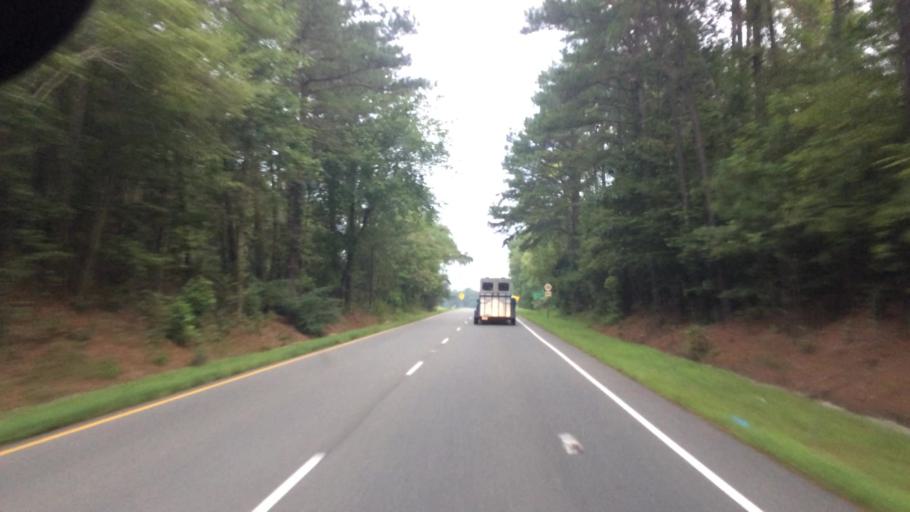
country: US
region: Virginia
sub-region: King William County
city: West Point
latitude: 37.4154
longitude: -76.8184
